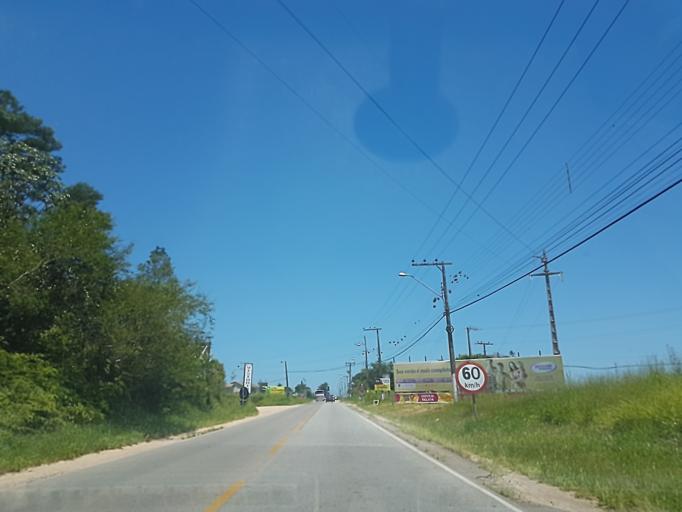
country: BR
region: Santa Catarina
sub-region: Jaguaruna
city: Jaguaruna
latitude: -28.6097
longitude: -49.0287
